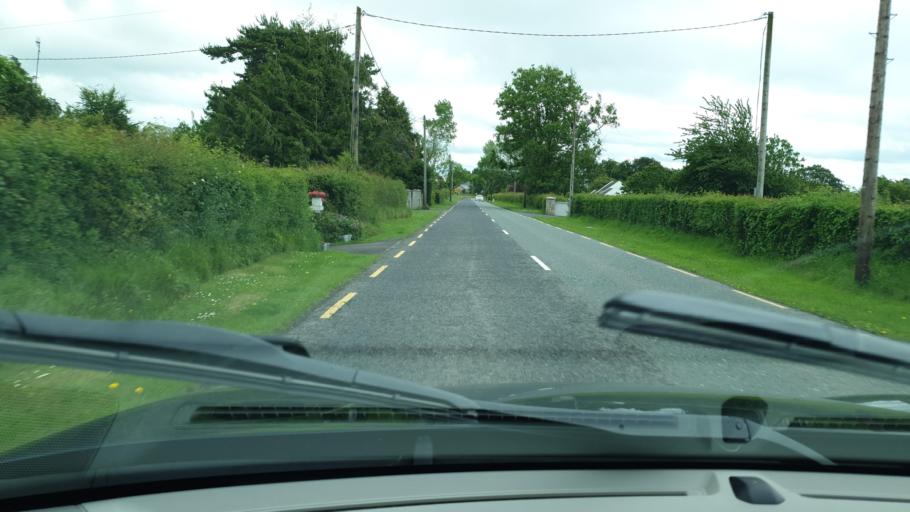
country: IE
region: Leinster
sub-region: An Mhi
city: Dunboyne
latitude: 53.4295
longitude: -6.5041
